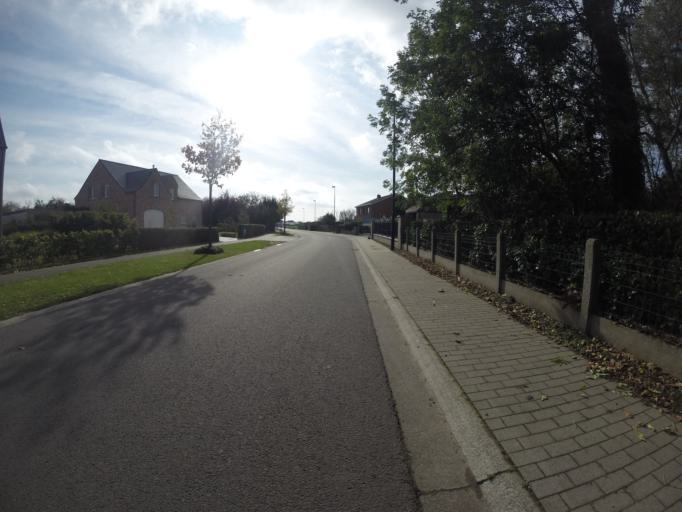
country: BE
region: Flanders
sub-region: Provincie Oost-Vlaanderen
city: Knesselare
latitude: 51.1315
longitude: 3.4171
